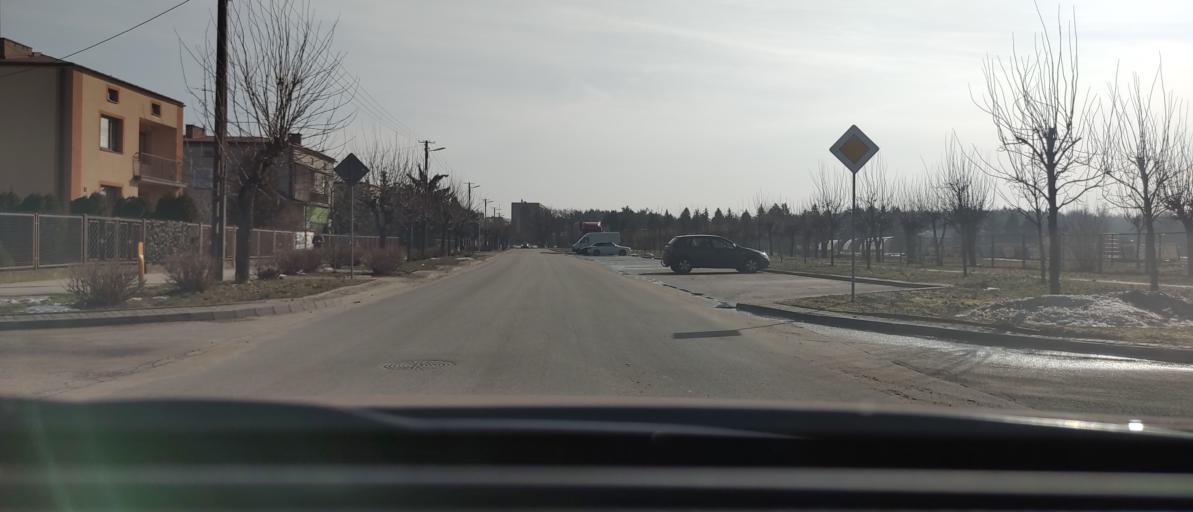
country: PL
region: Masovian Voivodeship
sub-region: Powiat bialobrzeski
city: Bialobrzegi
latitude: 51.6464
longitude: 20.9445
